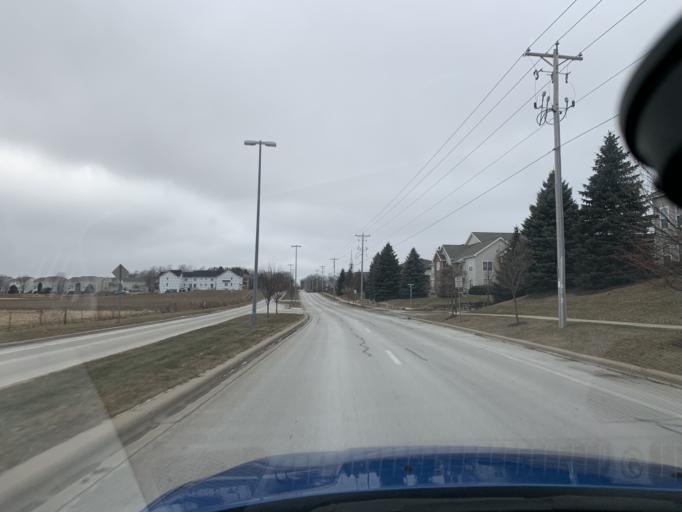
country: US
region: Wisconsin
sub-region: Dane County
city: Middleton
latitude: 43.0749
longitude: -89.5446
